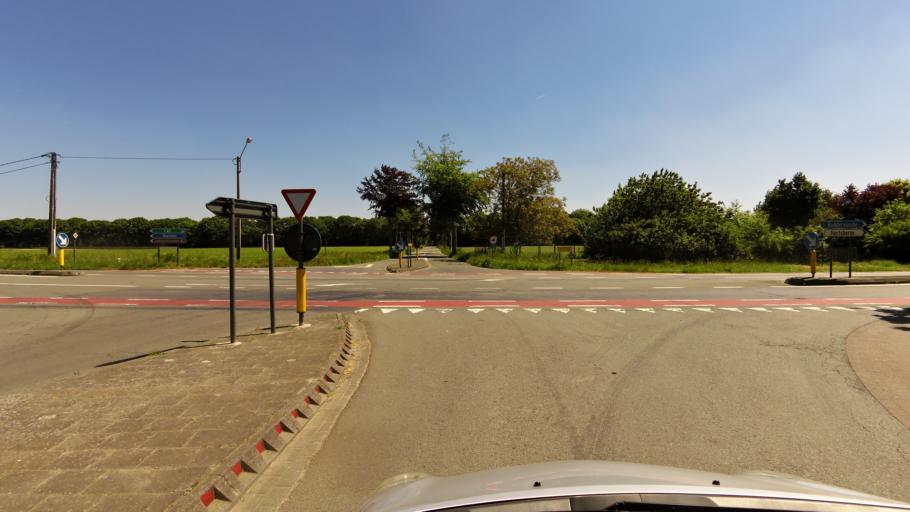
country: BE
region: Flanders
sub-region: Provincie West-Vlaanderen
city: Oostkamp
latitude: 51.1163
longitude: 3.2739
